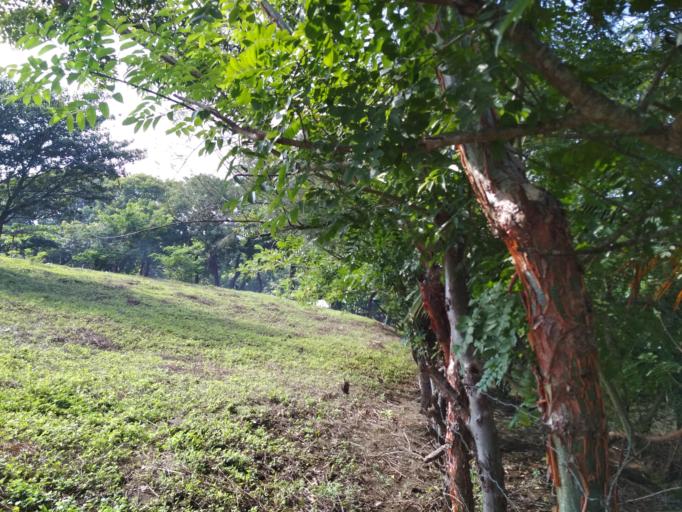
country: MX
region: Veracruz
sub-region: San Andres Tuxtla
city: Matacapan
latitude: 18.4423
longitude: -95.1726
